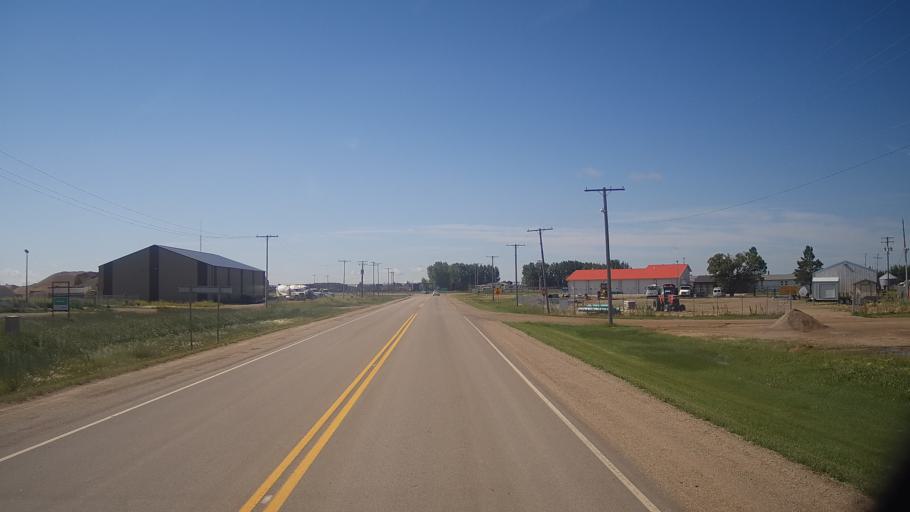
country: CA
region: Saskatchewan
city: Watrous
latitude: 51.6689
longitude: -105.4516
